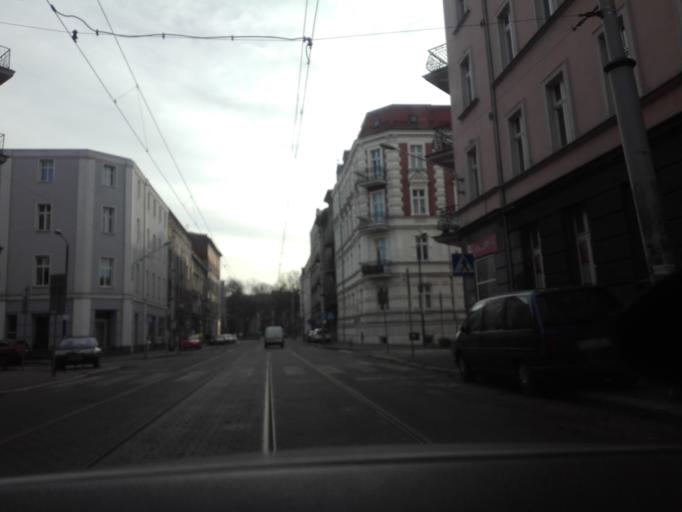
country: PL
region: Silesian Voivodeship
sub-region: Katowice
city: Katowice
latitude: 50.2608
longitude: 19.0108
